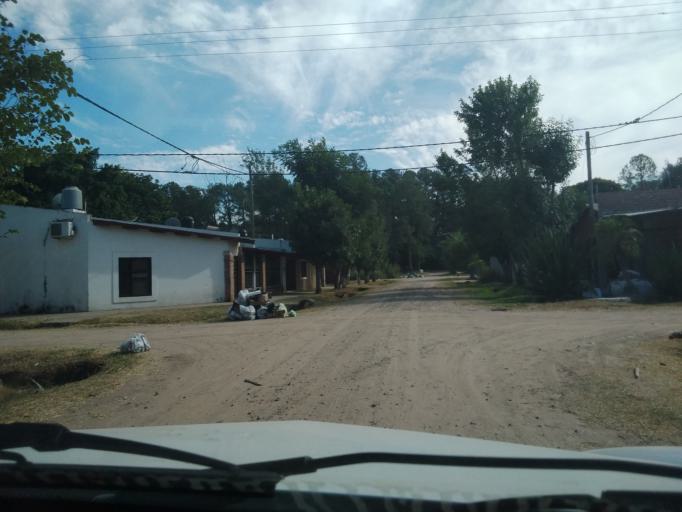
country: AR
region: Corrientes
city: Corrientes
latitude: -27.5099
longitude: -58.8024
